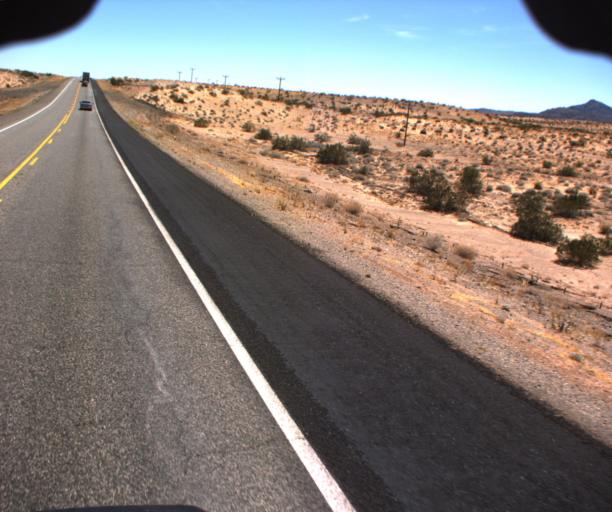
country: US
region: Arizona
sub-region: La Paz County
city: Parker
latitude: 34.0750
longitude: -114.2632
